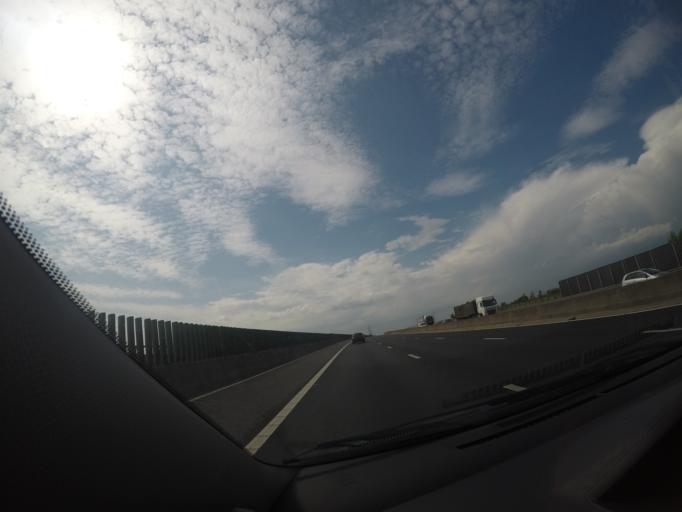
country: GB
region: Scotland
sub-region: Dumfries and Galloway
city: Gretna
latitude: 54.9793
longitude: -3.0210
